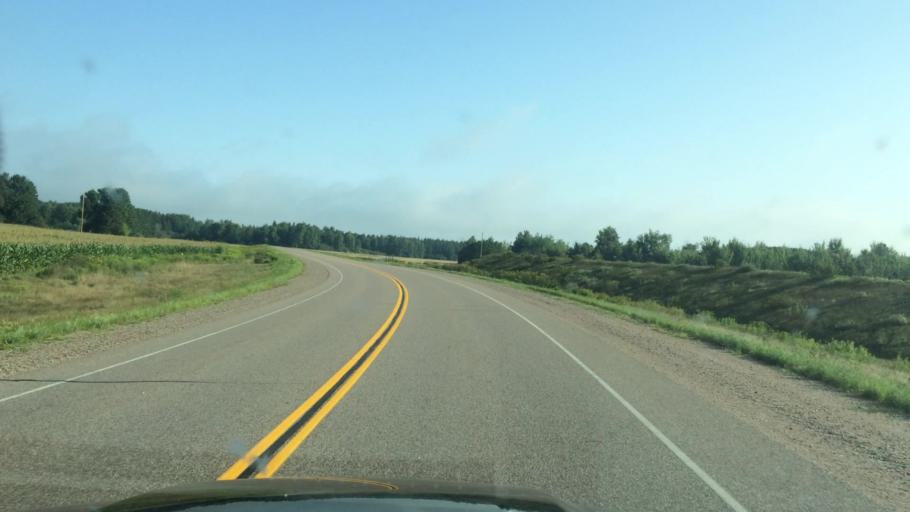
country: US
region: Wisconsin
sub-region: Langlade County
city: Antigo
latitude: 45.1447
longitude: -89.1848
